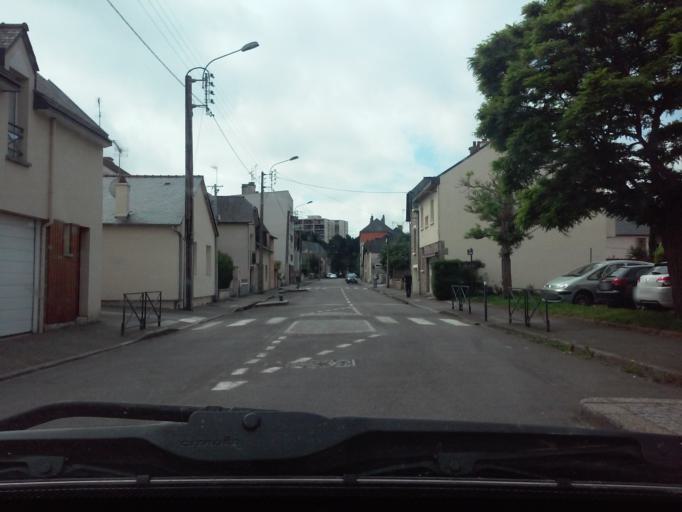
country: FR
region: Brittany
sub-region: Departement d'Ille-et-Vilaine
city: Rennes
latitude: 48.0922
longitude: -1.6855
